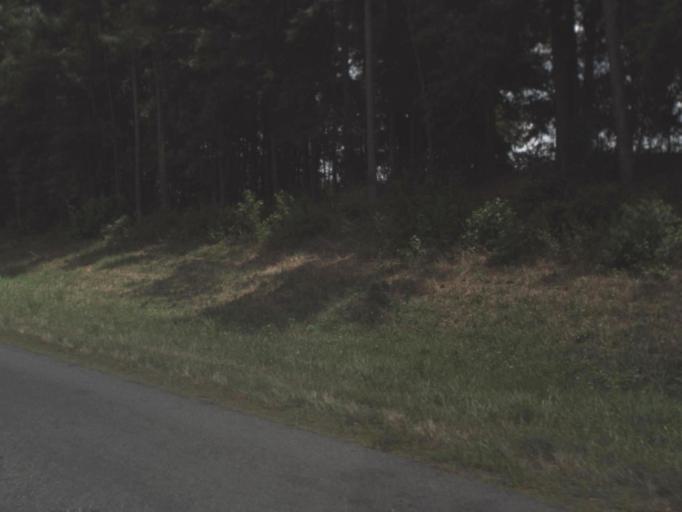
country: US
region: Florida
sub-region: Hamilton County
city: Jasper
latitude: 30.4929
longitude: -83.0292
